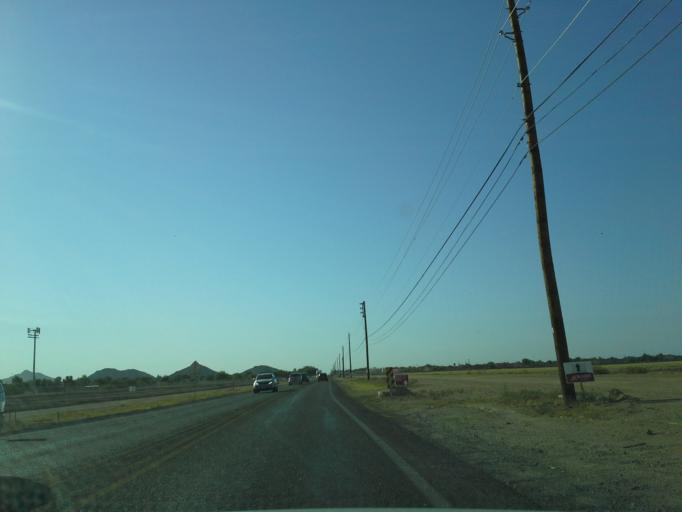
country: US
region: Arizona
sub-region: Pinal County
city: San Tan Valley
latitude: 33.1472
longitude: -111.5507
